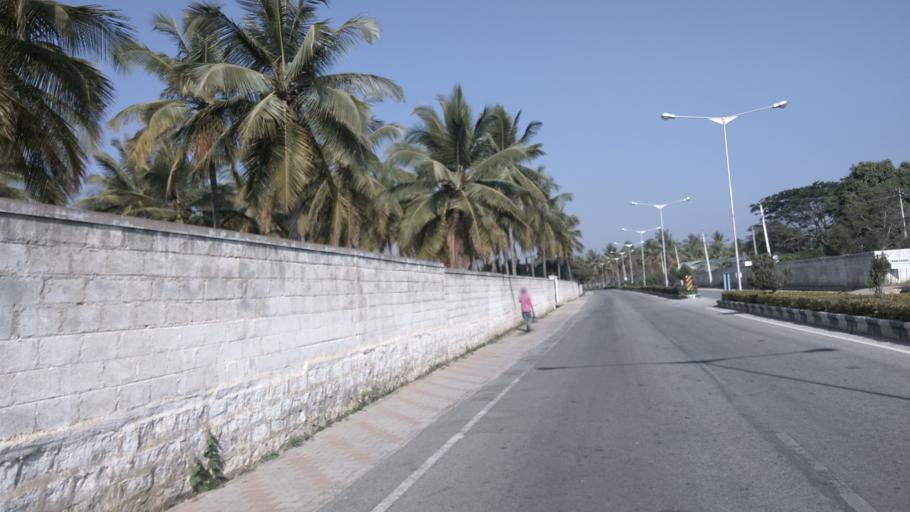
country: IN
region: Karnataka
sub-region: Bangalore Rural
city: Devanhalli
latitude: 13.1970
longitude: 77.6424
